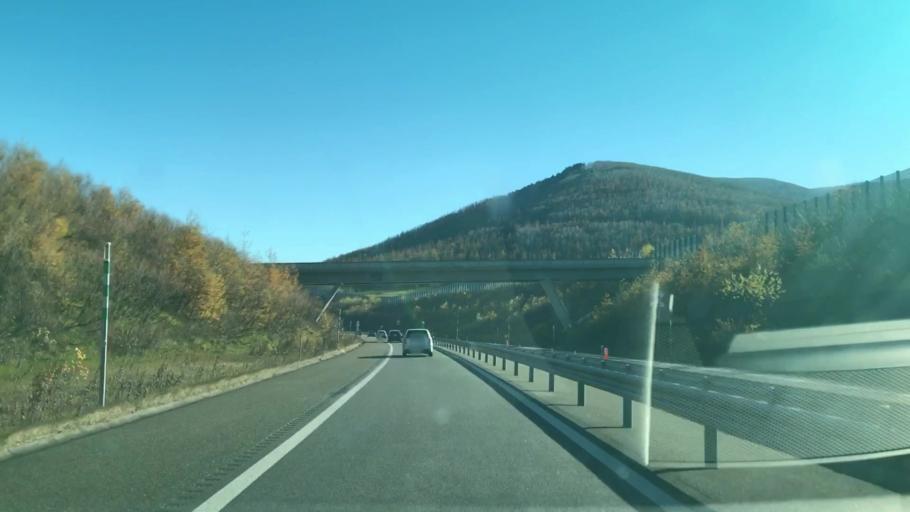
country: JP
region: Hokkaido
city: Otofuke
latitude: 43.0415
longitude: 142.7839
